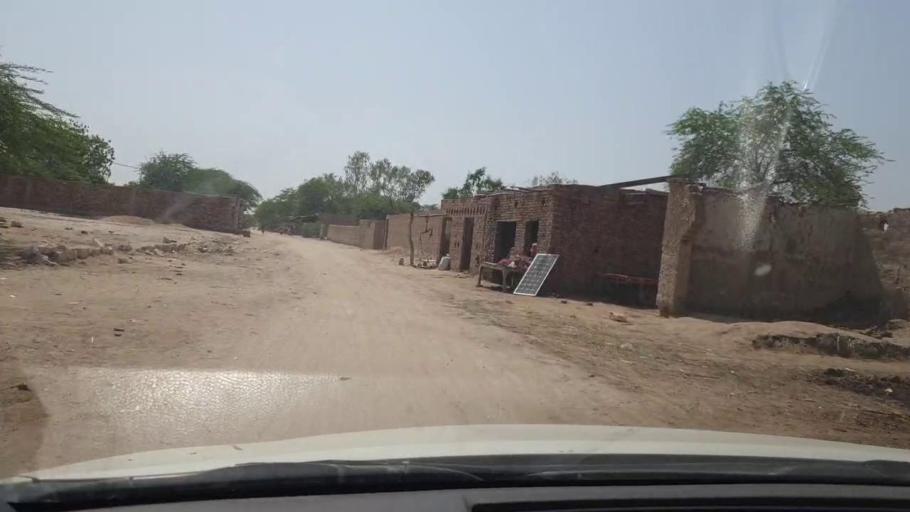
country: PK
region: Sindh
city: Rohri
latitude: 27.5217
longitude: 69.0530
